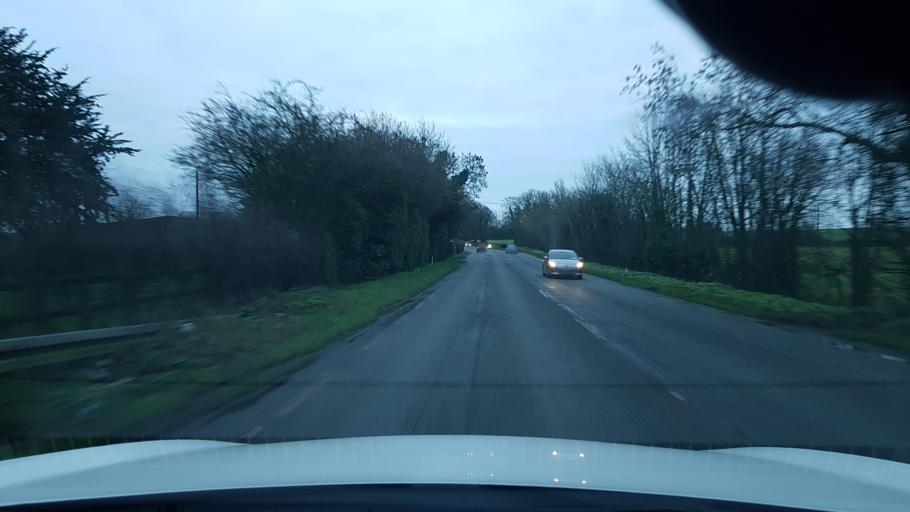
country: IE
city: Kentstown
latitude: 53.5861
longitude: -6.5934
